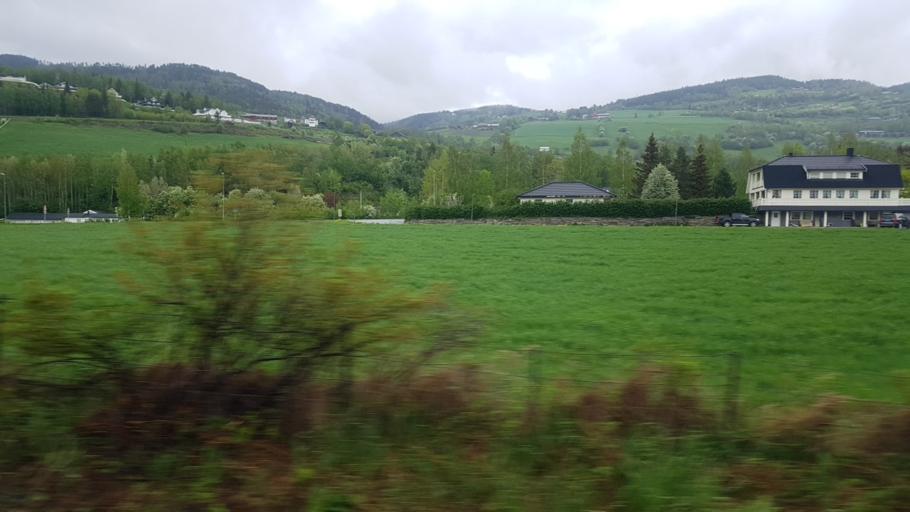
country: NO
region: Oppland
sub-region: Nord-Fron
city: Vinstra
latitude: 61.5796
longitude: 9.7651
